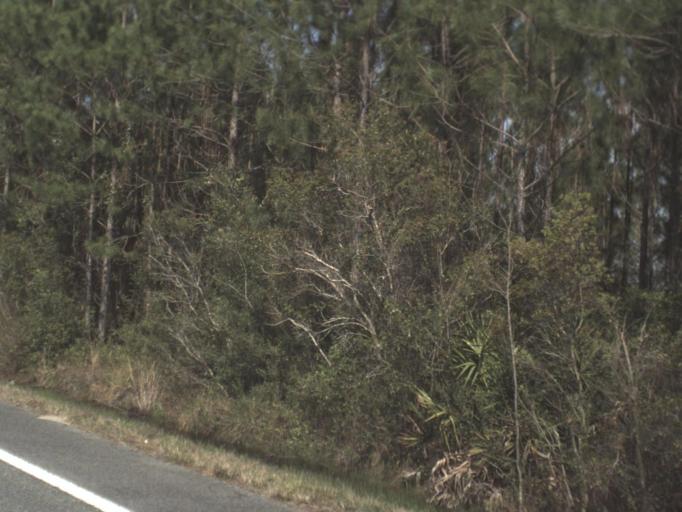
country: US
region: Florida
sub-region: Franklin County
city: Carrabelle
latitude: 29.9721
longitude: -84.4987
